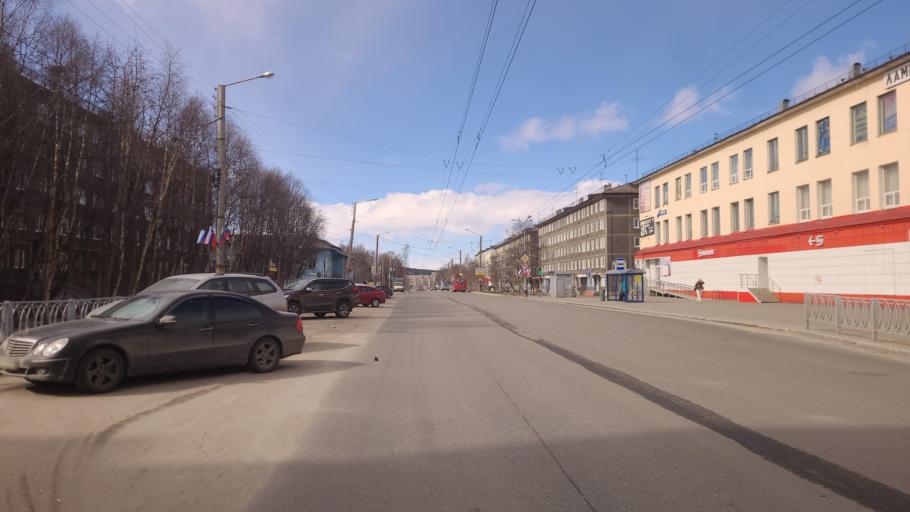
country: RU
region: Murmansk
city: Murmansk
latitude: 68.9516
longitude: 33.0745
